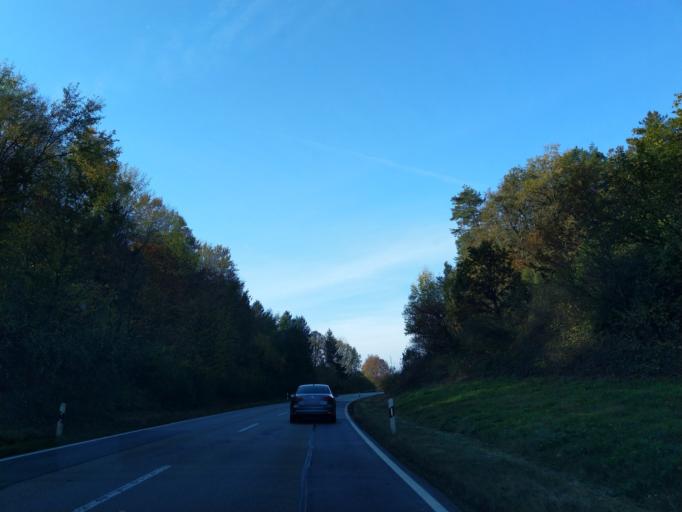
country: DE
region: Bavaria
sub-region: Lower Bavaria
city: Grattersdorf
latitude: 48.8178
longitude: 13.1301
